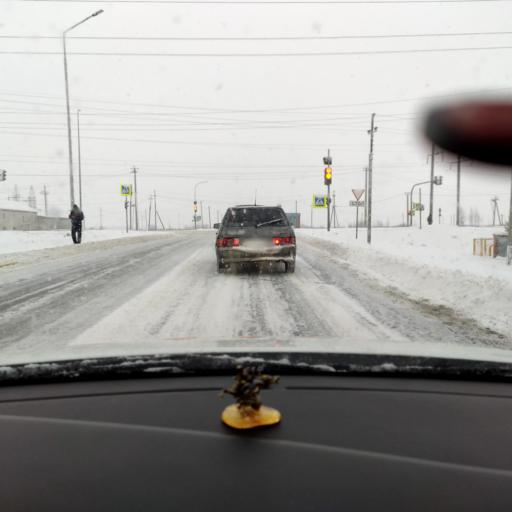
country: RU
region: Tatarstan
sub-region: Arskiy Rayon
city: Arsk
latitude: 56.1044
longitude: 49.8749
